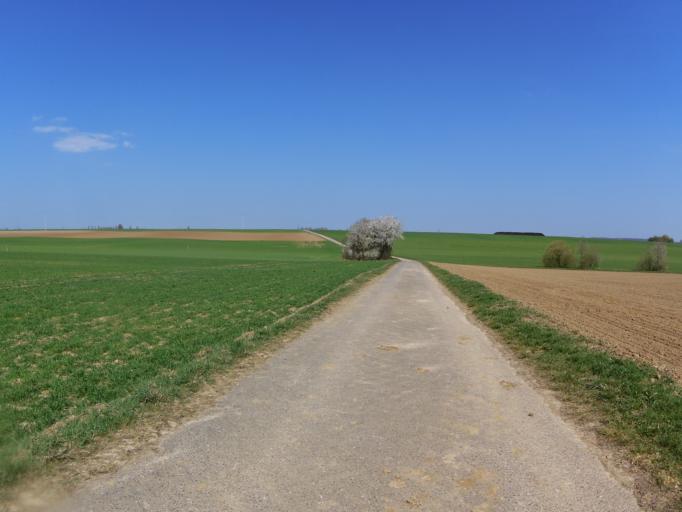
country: DE
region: Bavaria
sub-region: Regierungsbezirk Unterfranken
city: Mainstockheim
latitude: 49.8104
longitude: 10.1124
